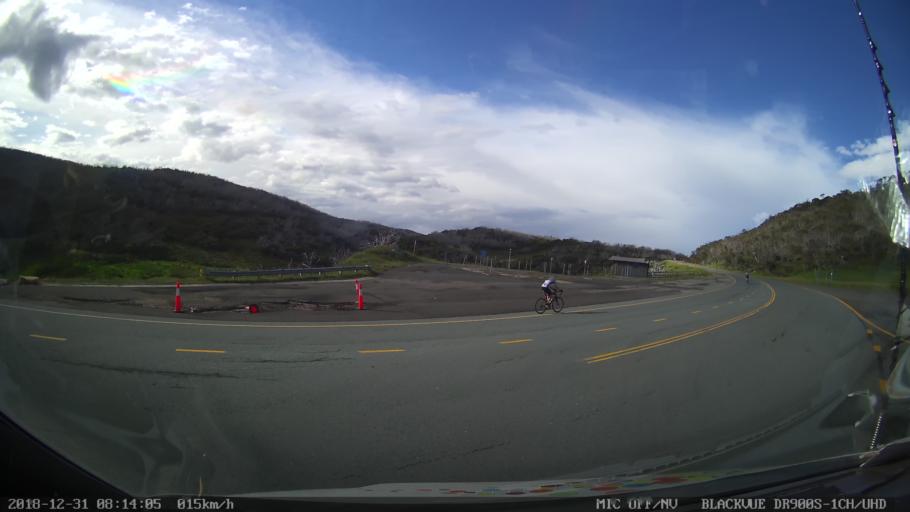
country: AU
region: New South Wales
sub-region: Snowy River
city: Jindabyne
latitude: -36.3942
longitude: 148.4274
